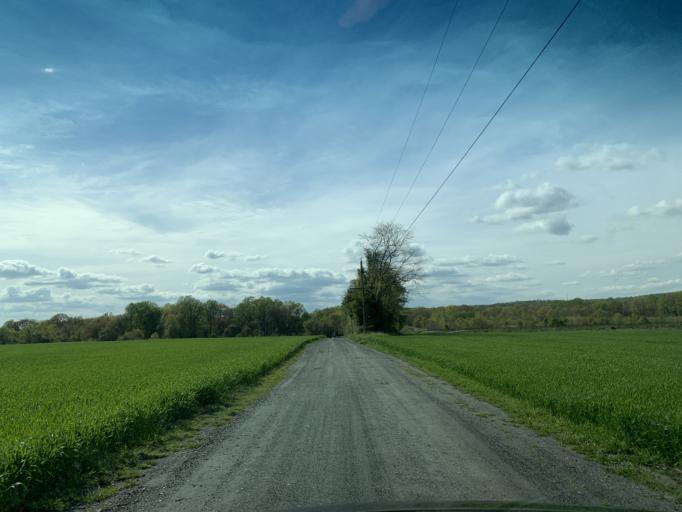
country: US
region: Maryland
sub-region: Harford County
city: Perryman
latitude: 39.4706
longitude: -76.2144
